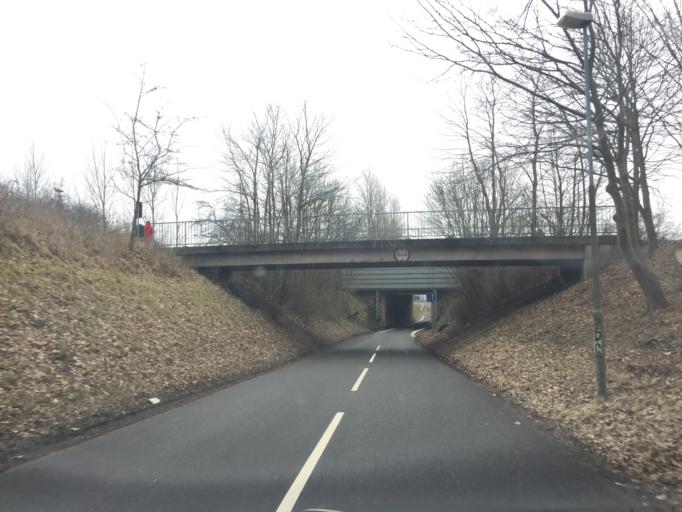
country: DK
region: Capital Region
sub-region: Hoje-Taastrup Kommune
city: Flong
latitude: 55.6456
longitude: 12.2211
